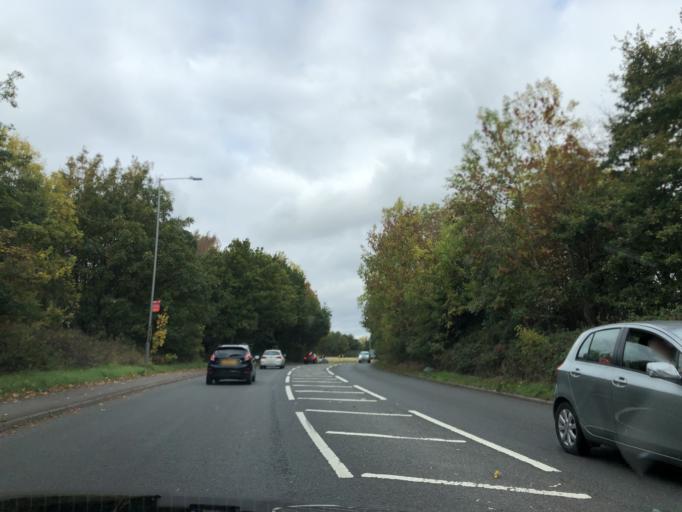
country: GB
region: England
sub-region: Warwickshire
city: Kenilworth
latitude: 52.3285
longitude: -1.5601
